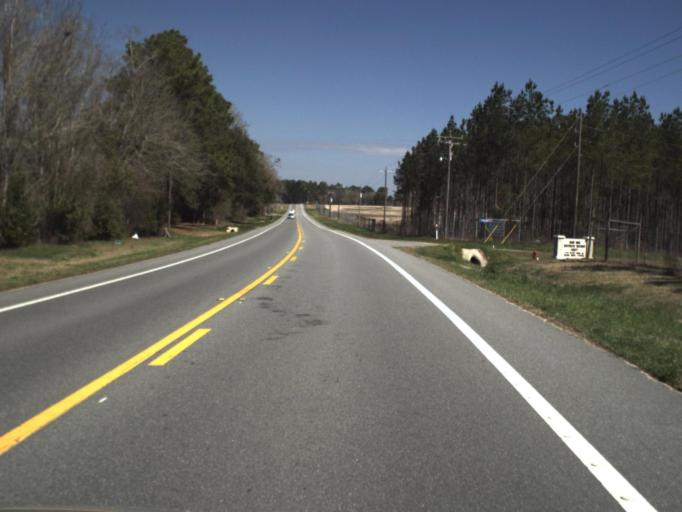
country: US
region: Florida
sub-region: Jackson County
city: Sneads
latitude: 30.6869
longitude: -85.0246
